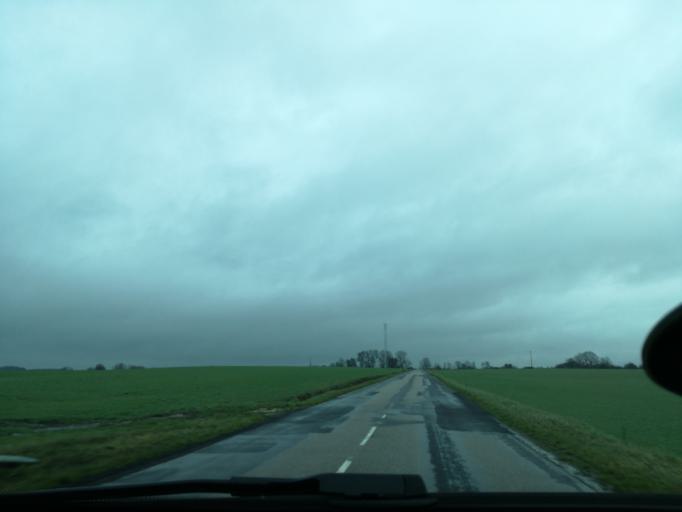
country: FR
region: Lorraine
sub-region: Departement de la Meuse
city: Clermont-en-Argonne
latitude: 48.9953
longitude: 5.0876
